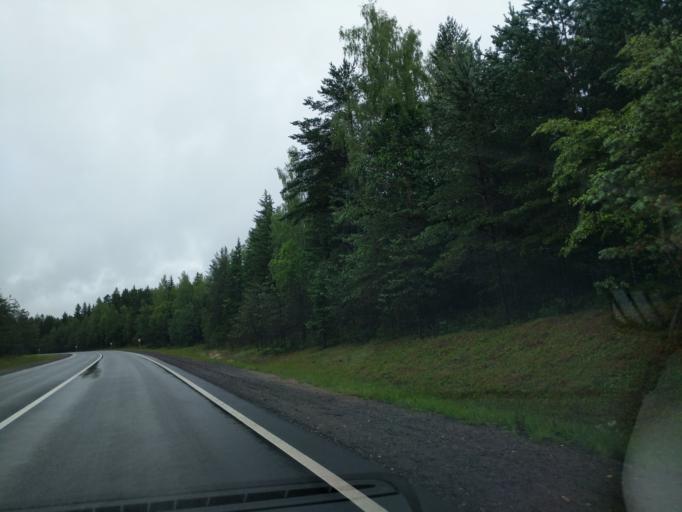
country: BY
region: Minsk
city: Syomkava
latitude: 54.1932
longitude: 27.4998
